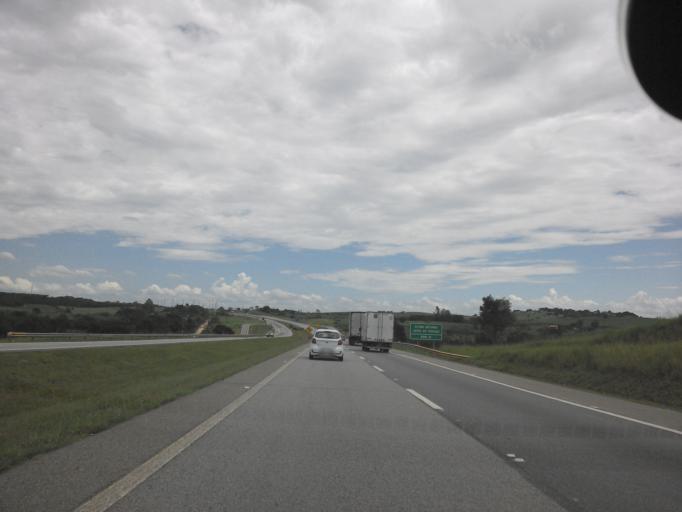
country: BR
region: Sao Paulo
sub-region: Cacapava
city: Cacapava
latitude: -23.1478
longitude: -45.6847
